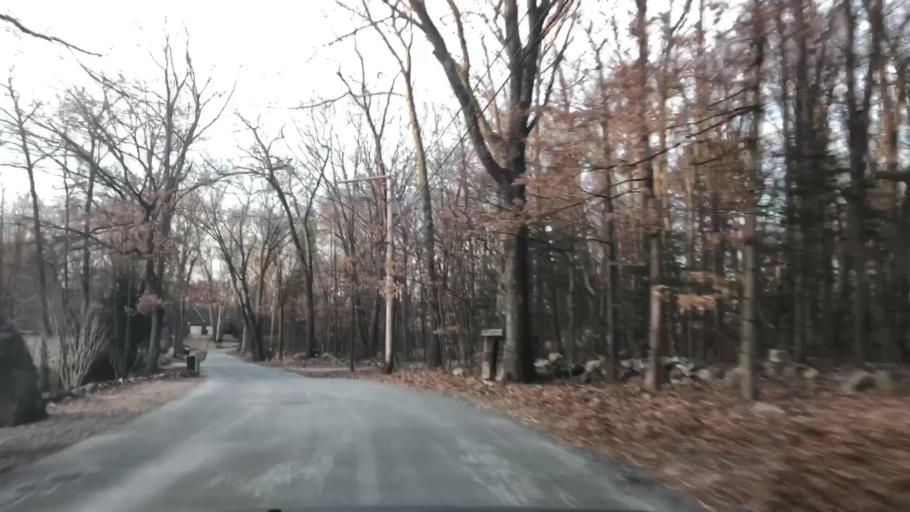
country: US
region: Massachusetts
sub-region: Essex County
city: North Andover
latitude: 42.6934
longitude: -71.0761
